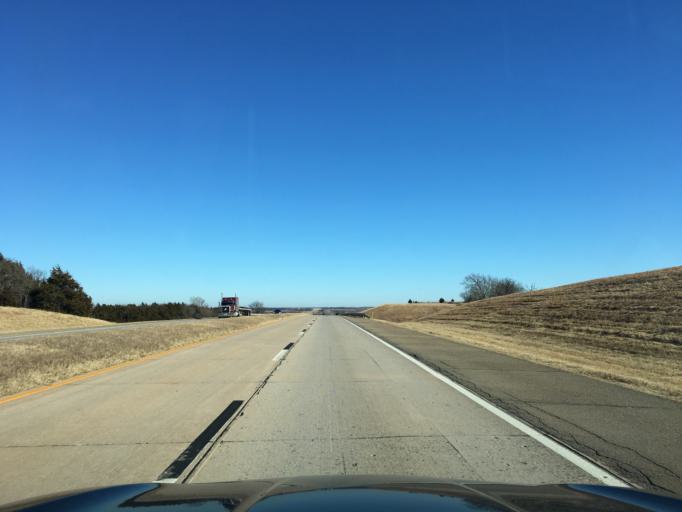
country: US
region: Oklahoma
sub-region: Payne County
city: Yale
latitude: 36.2240
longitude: -96.7327
